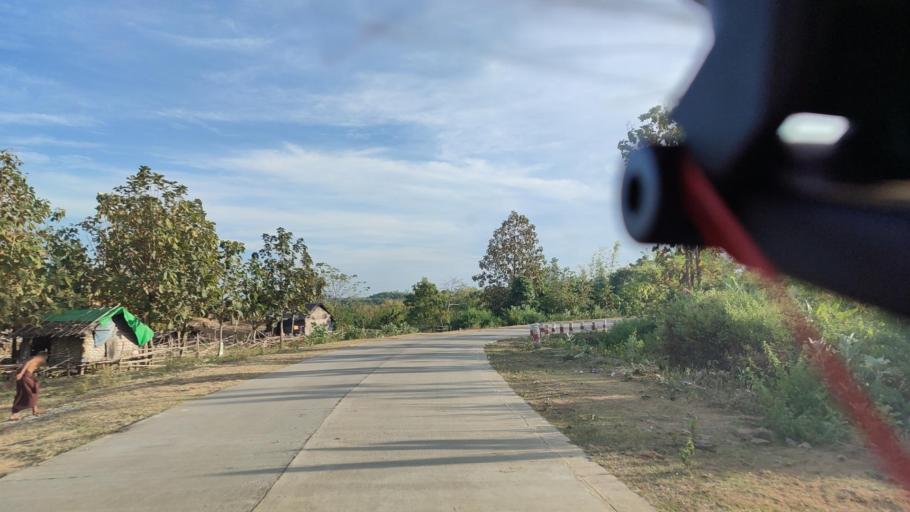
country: MM
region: Magway
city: Taungdwingyi
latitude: 20.0189
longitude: 95.8281
